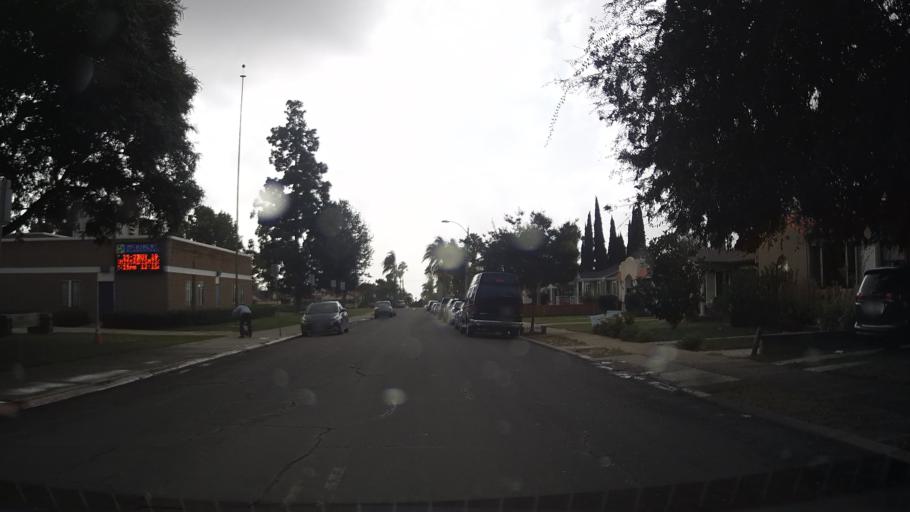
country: US
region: California
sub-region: San Diego County
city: San Diego
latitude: 32.7372
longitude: -117.1222
